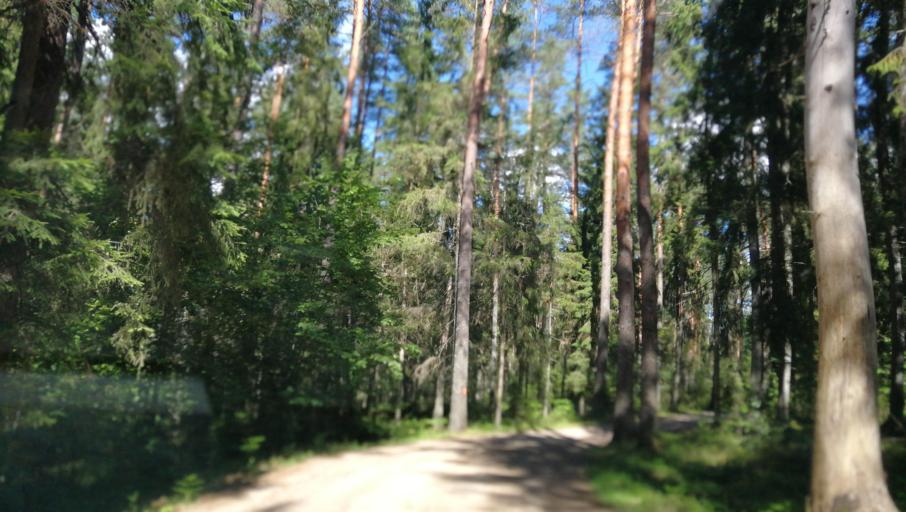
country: LV
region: Cesu Rajons
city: Cesis
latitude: 57.2917
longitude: 25.2128
